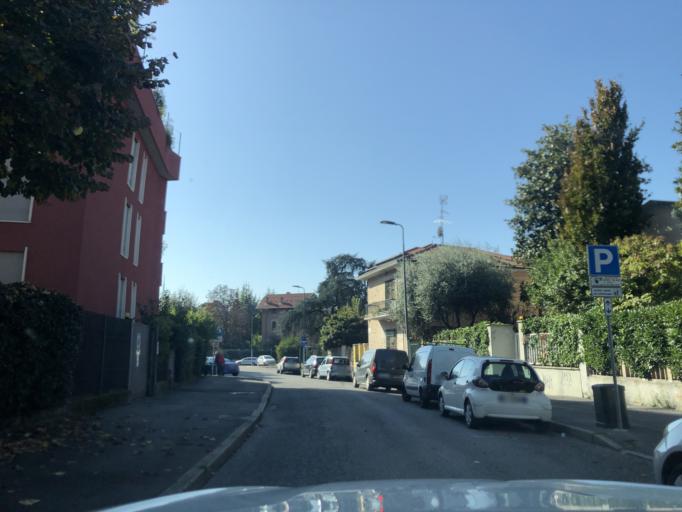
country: IT
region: Lombardy
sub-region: Citta metropolitana di Milano
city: Milano
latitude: 45.4979
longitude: 9.1985
